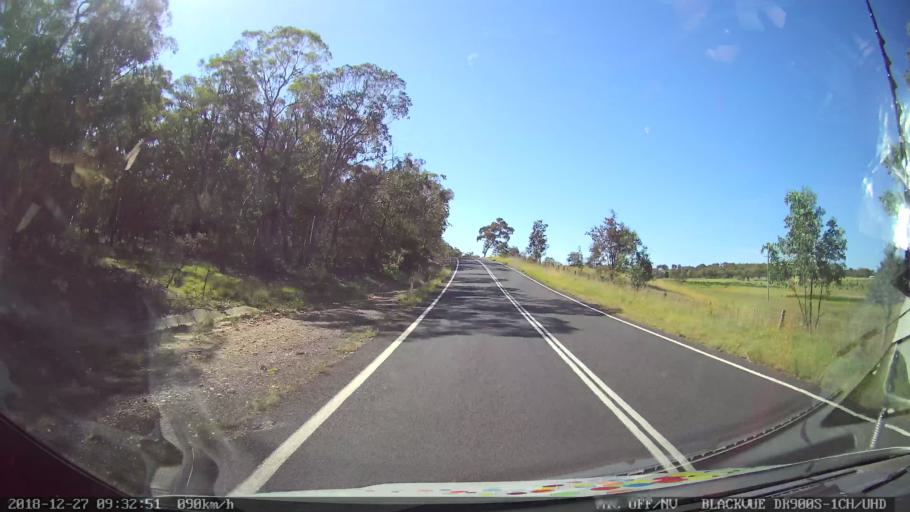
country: AU
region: New South Wales
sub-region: Lithgow
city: Portland
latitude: -33.2126
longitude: 150.0179
